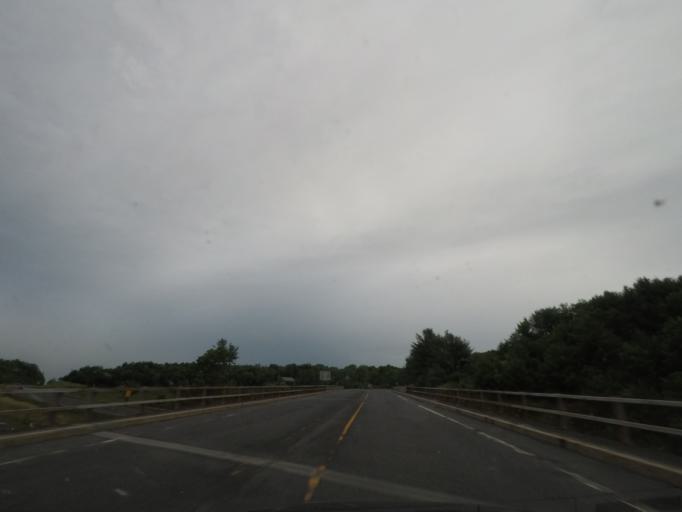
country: US
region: New York
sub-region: Columbia County
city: Chatham
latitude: 42.4202
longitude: -73.5487
